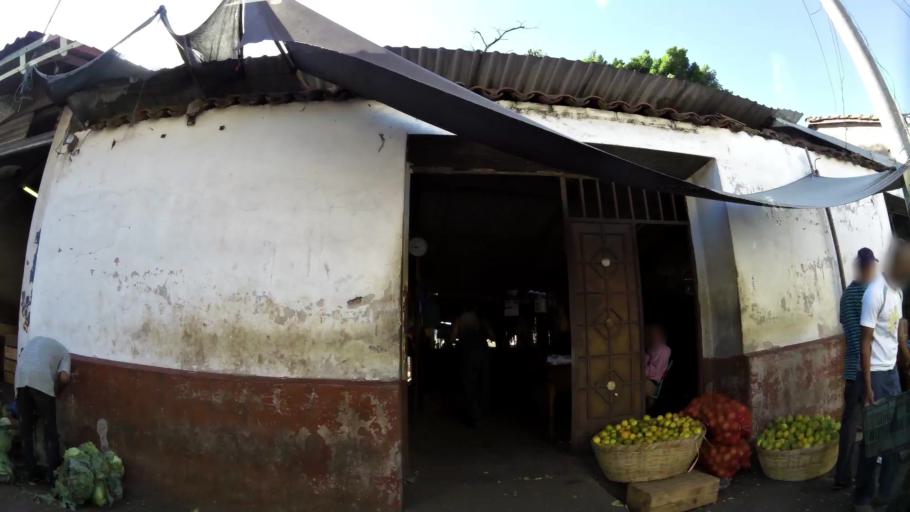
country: SV
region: San Miguel
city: San Miguel
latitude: 13.4792
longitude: -88.1793
